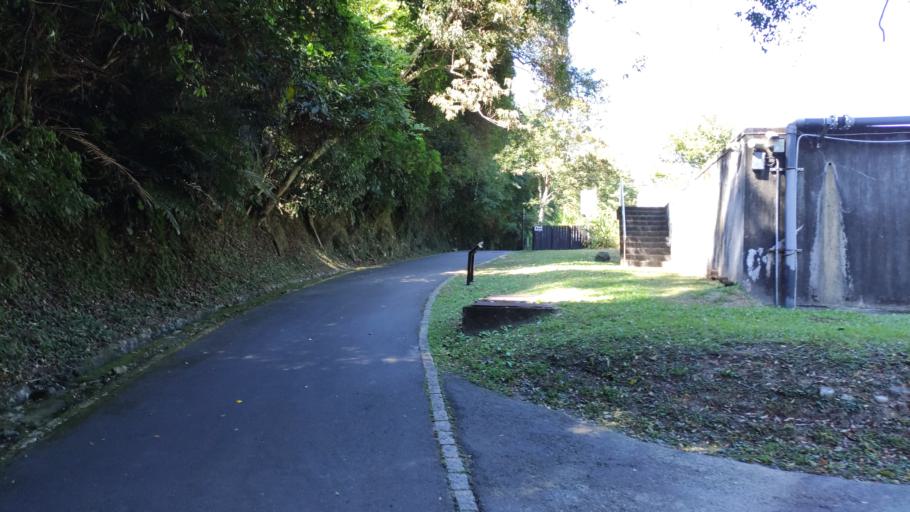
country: TW
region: Taiwan
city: Daxi
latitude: 24.8425
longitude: 121.3034
